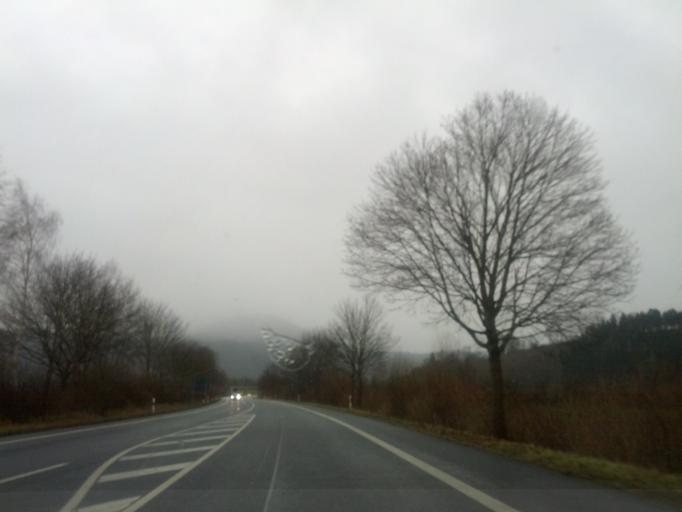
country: DE
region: Hesse
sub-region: Regierungsbezirk Kassel
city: Bad Sooden-Allendorf
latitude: 51.2607
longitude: 9.9829
